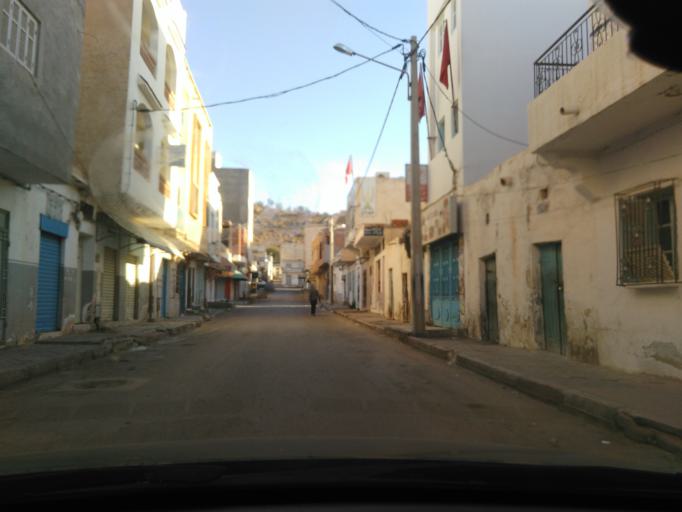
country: TN
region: Tataouine
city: Tataouine
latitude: 32.9281
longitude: 10.4502
